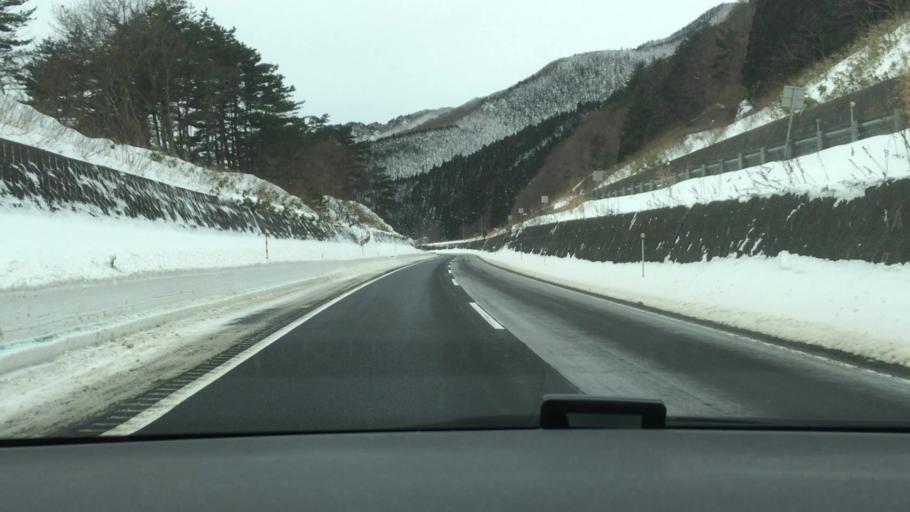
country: JP
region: Akita
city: Hanawa
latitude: 40.1223
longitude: 140.8424
